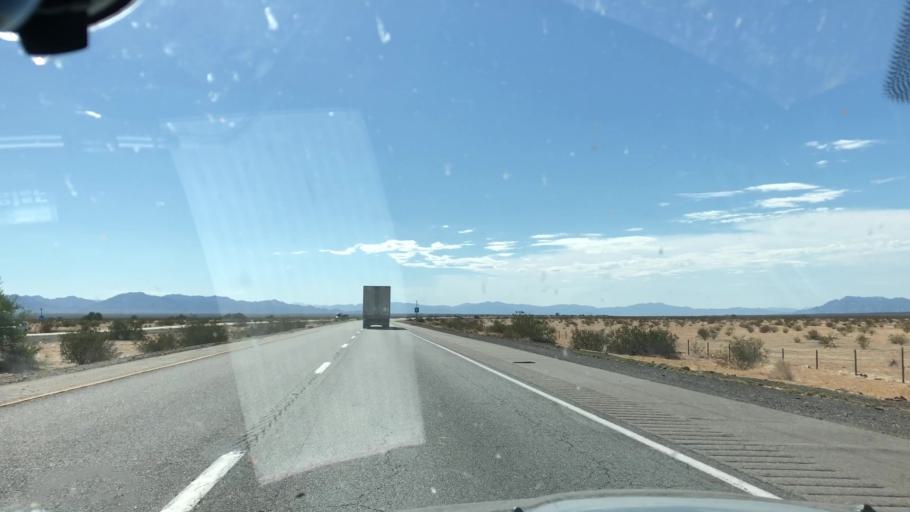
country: US
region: California
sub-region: Riverside County
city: Mesa Verde
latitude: 33.6297
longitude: -115.0696
